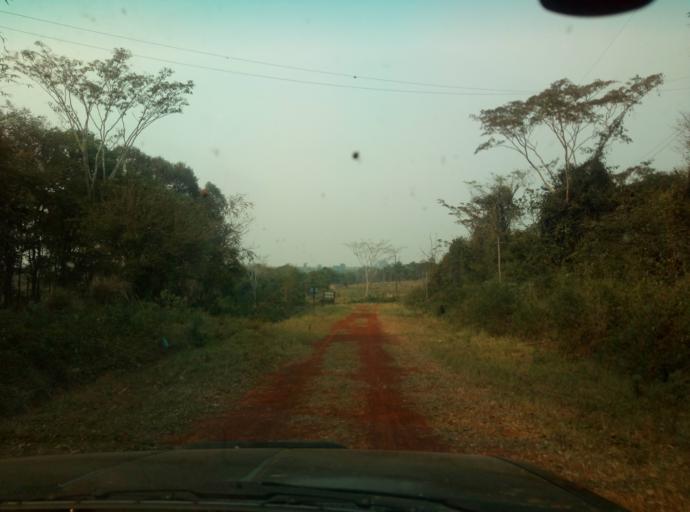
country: PY
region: Caaguazu
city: Carayao
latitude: -25.2095
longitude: -56.2241
